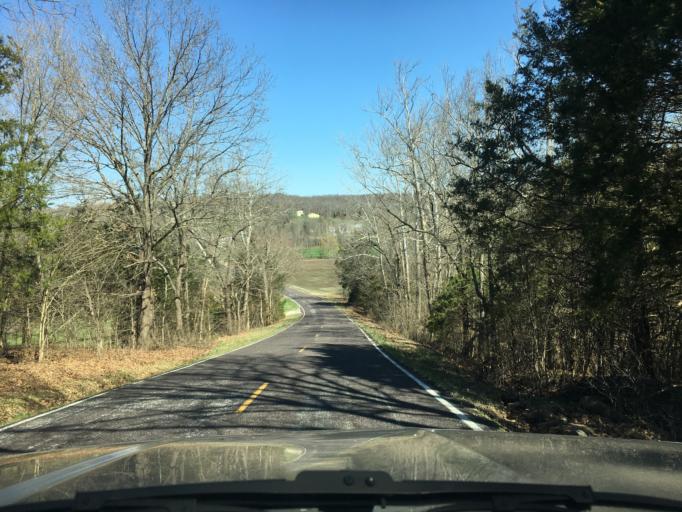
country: US
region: Missouri
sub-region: Franklin County
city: Gerald
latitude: 38.5243
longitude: -91.3298
